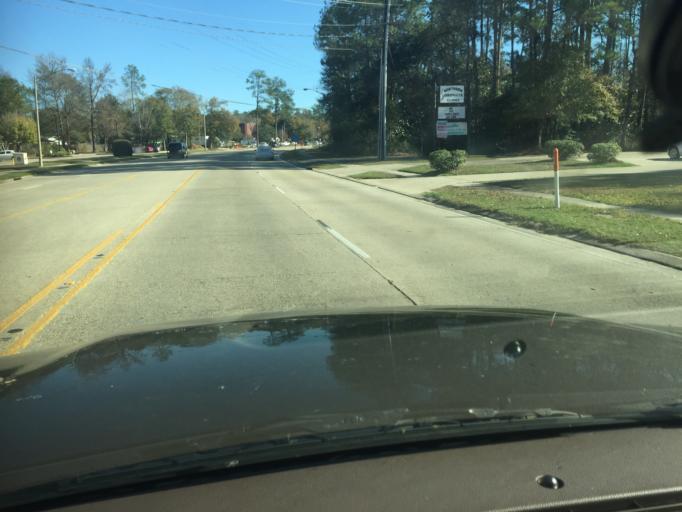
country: US
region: Louisiana
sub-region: Saint Tammany Parish
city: Slidell
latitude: 30.2983
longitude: -89.7601
